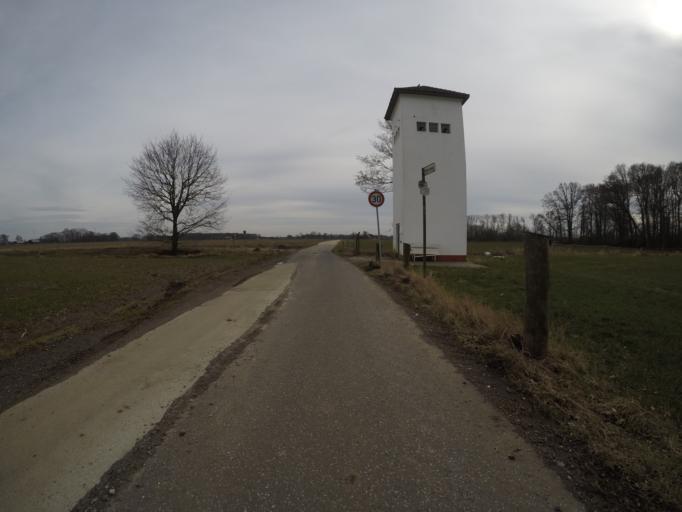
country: DE
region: North Rhine-Westphalia
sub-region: Regierungsbezirk Dusseldorf
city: Mehrhoog
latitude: 51.7882
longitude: 6.5436
